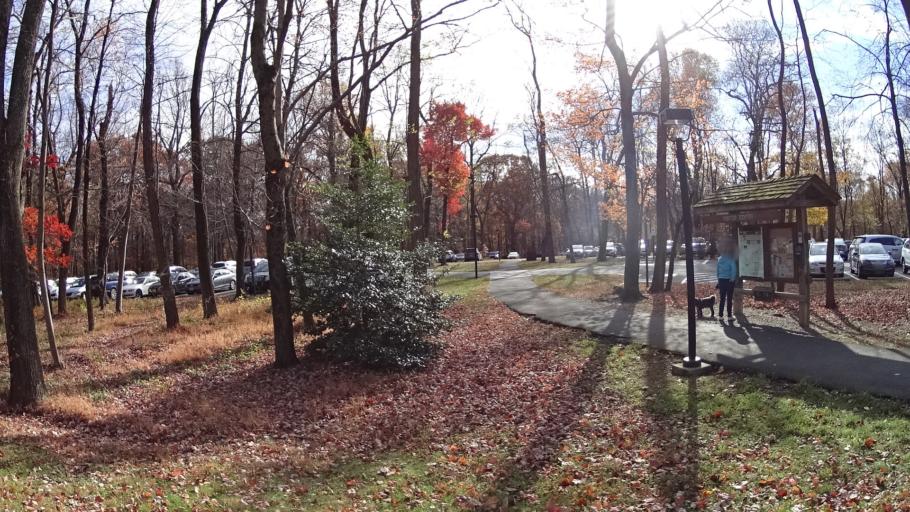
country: US
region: New Jersey
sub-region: Somerset County
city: Bernardsville
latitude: 40.7619
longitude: -74.5424
